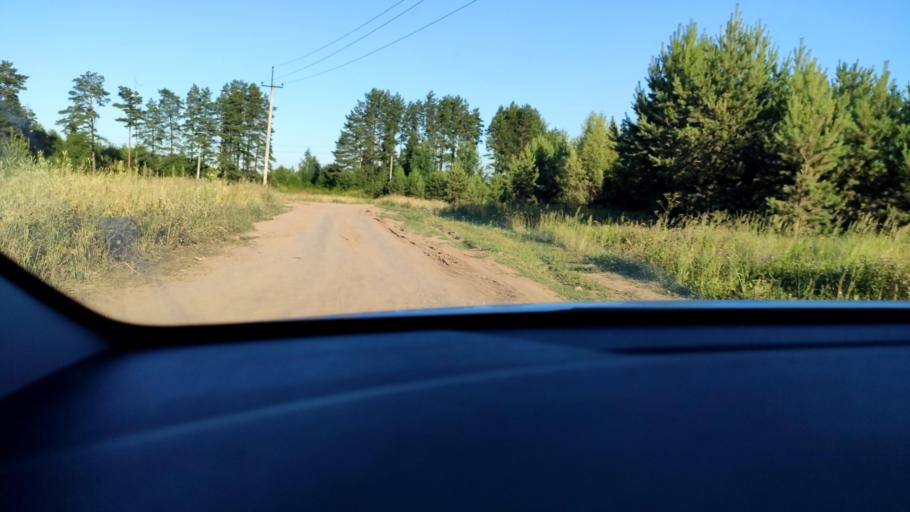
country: RU
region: Tatarstan
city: Vysokaya Gora
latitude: 55.8208
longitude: 49.2494
